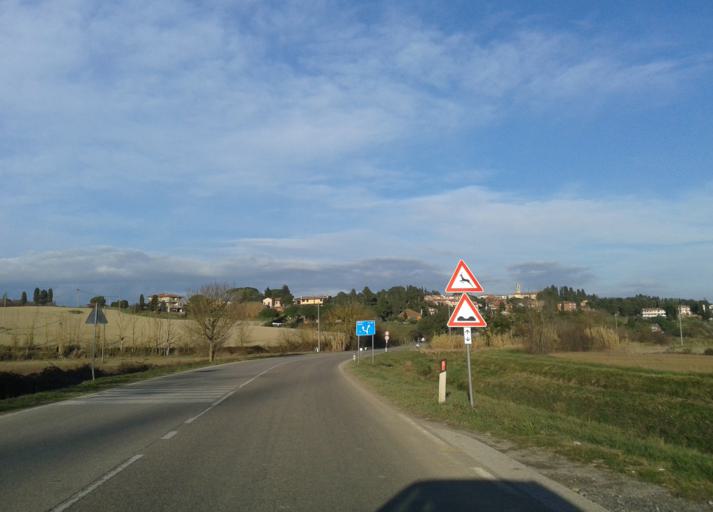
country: IT
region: Tuscany
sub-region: Provincia di Livorno
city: Guasticce
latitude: 43.5724
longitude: 10.4307
